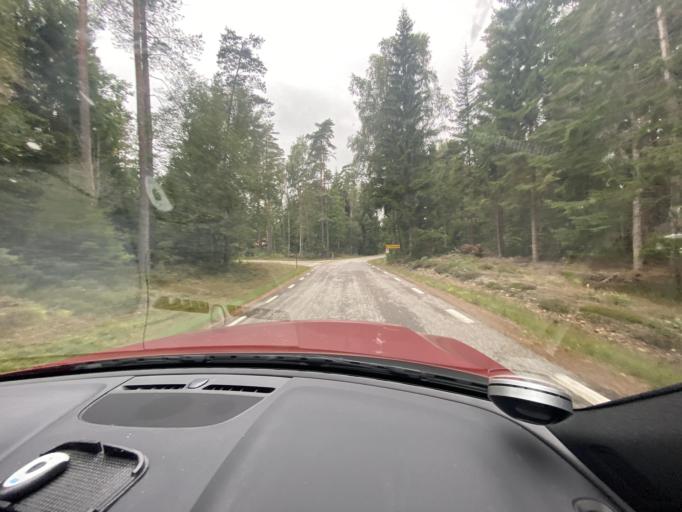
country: SE
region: Kronoberg
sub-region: Markaryds Kommun
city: Markaryd
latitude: 56.4975
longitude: 13.5697
